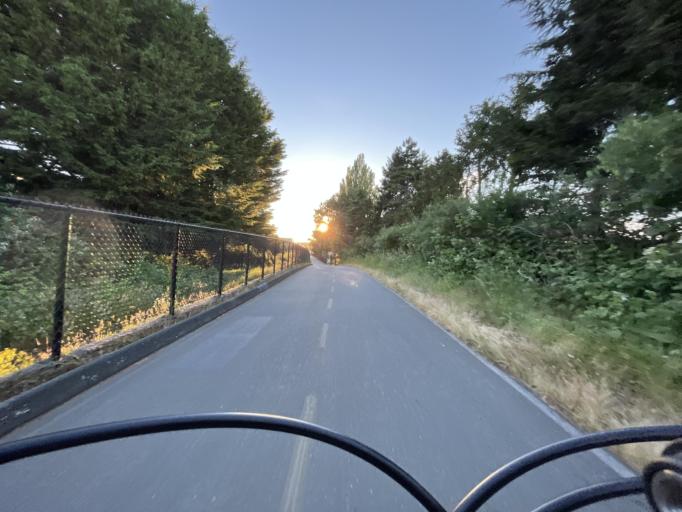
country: CA
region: British Columbia
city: Victoria
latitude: 48.4333
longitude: -123.3910
